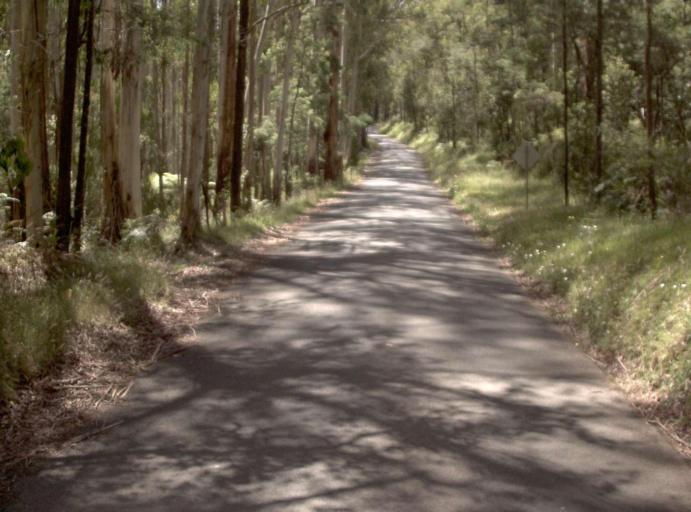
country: AU
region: Victoria
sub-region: Baw Baw
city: Warragul
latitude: -37.8623
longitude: 146.0056
